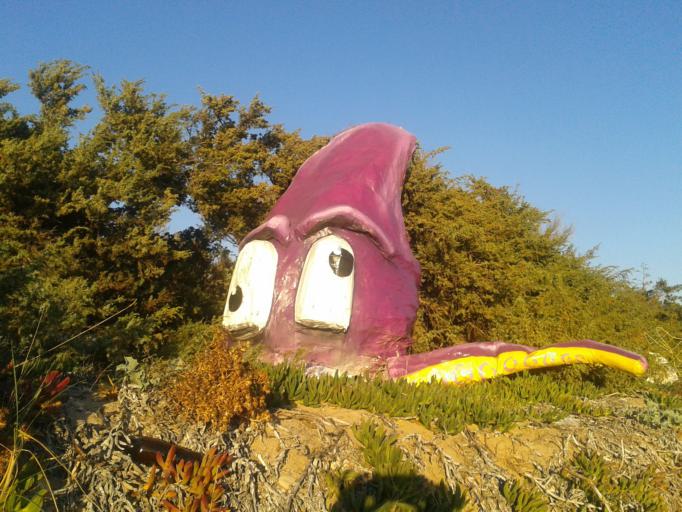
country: IT
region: Sicily
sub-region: Ragusa
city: Santa Croce Camerina
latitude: 36.7869
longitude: 14.4969
